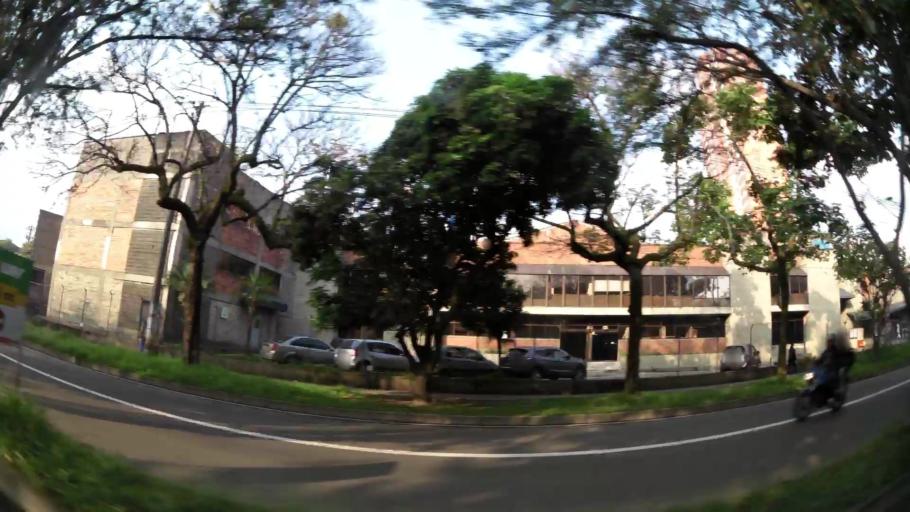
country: CO
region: Antioquia
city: Sabaneta
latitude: 6.1669
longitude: -75.6179
